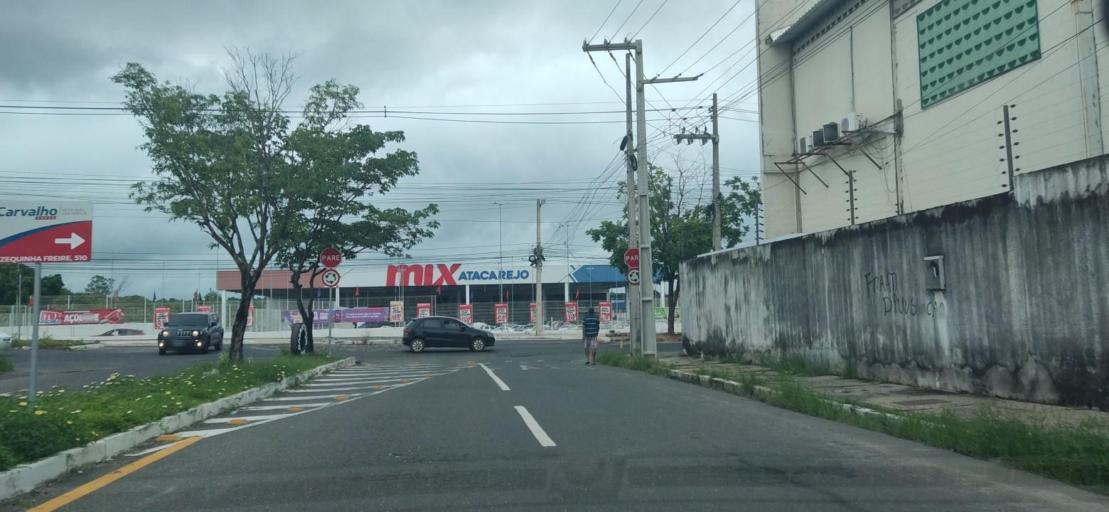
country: BR
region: Piaui
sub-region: Teresina
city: Teresina
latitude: -5.0654
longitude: -42.7495
